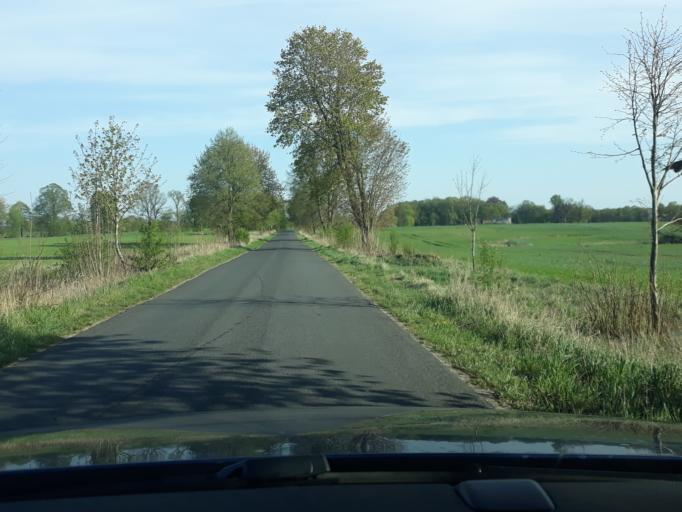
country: PL
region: Pomeranian Voivodeship
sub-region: Powiat czluchowski
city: Przechlewo
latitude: 53.8506
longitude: 17.3546
